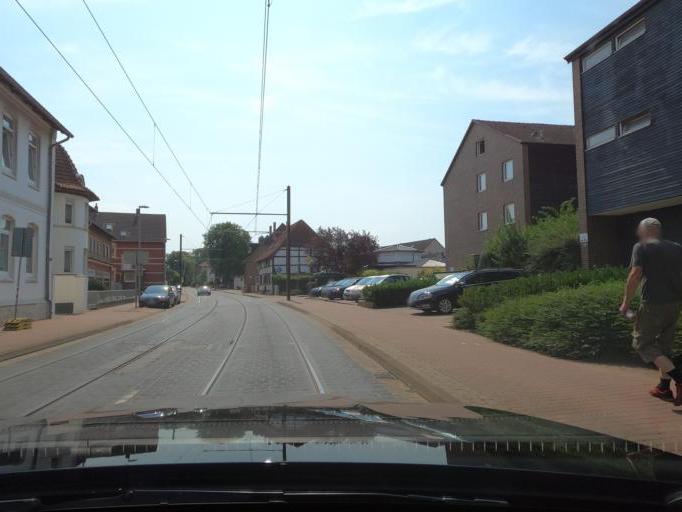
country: DE
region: Lower Saxony
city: Sarstedt
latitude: 52.2729
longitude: 9.8395
